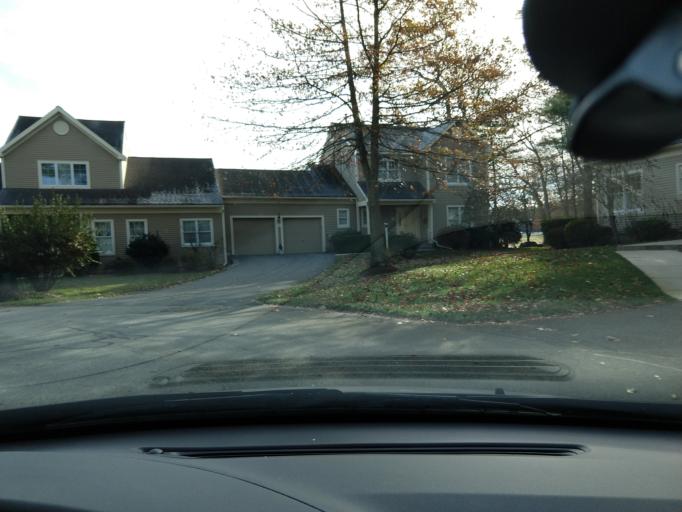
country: US
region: Massachusetts
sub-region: Middlesex County
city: Bedford
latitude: 42.5128
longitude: -71.2927
